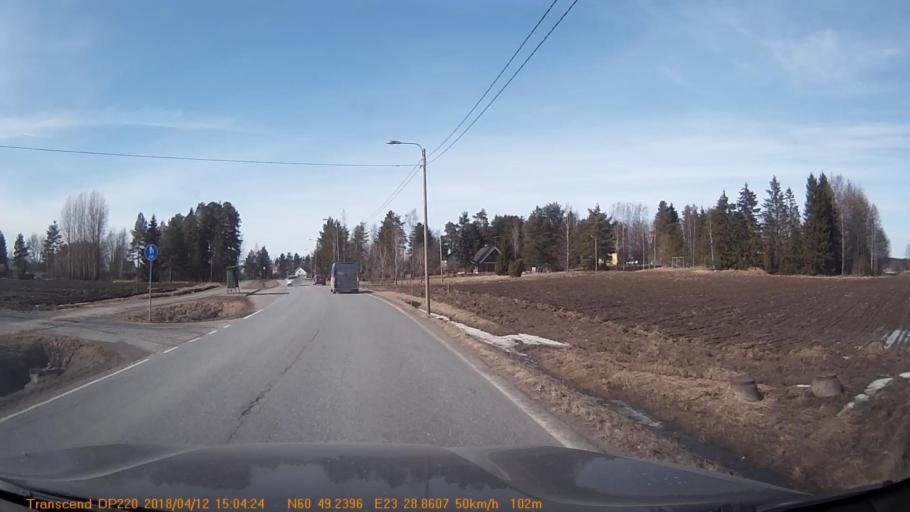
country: FI
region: Haeme
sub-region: Forssa
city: Jokioinen
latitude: 60.8208
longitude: 23.4809
